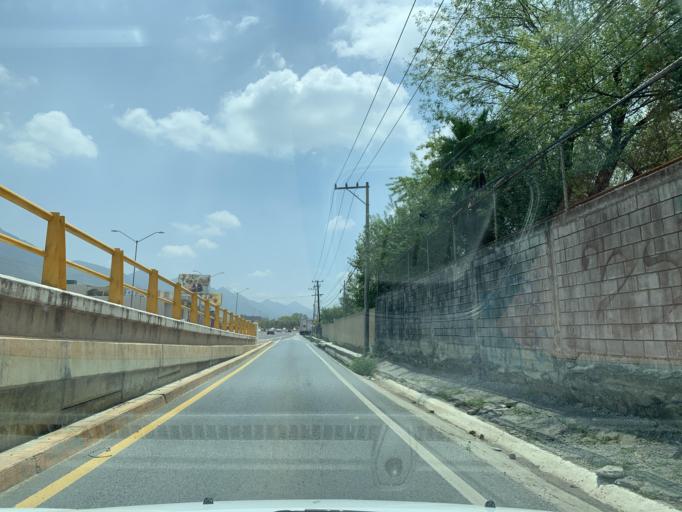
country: MX
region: Nuevo Leon
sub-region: Juarez
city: Bosques de San Pedro
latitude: 25.5219
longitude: -100.2049
